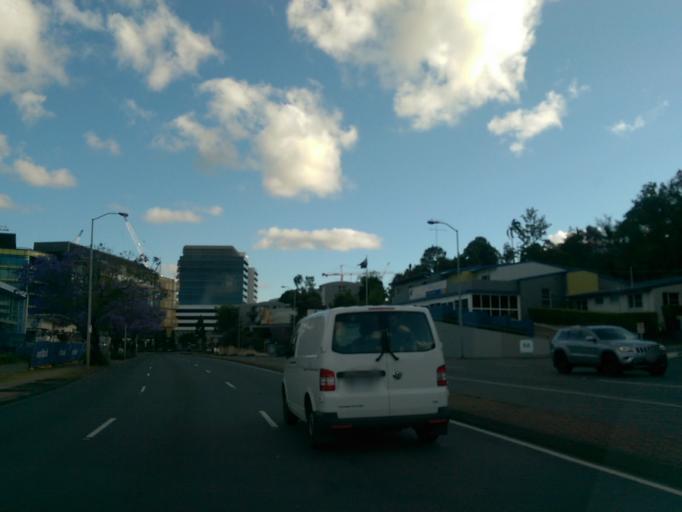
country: AU
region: Queensland
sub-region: Brisbane
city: Fortitude Valley
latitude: -27.4470
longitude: 153.0425
